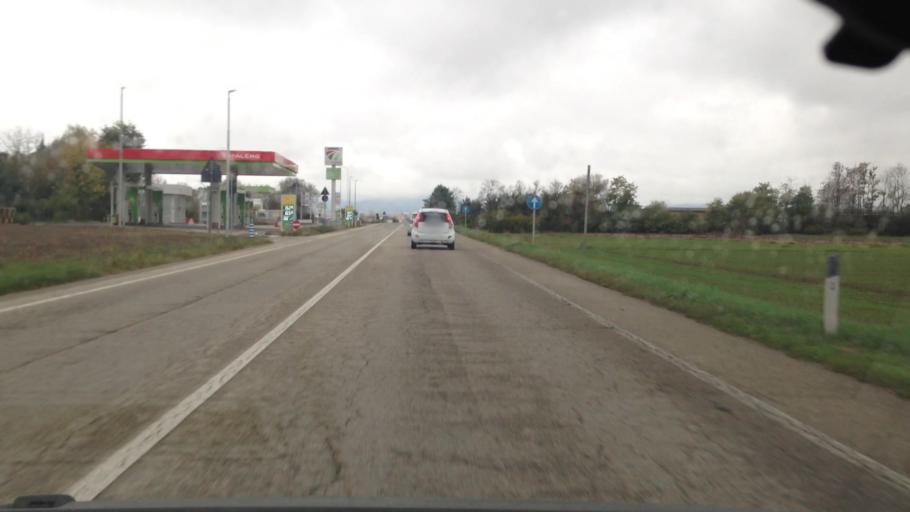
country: IT
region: Piedmont
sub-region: Provincia di Torino
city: Riva Presso Chieri
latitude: 44.9905
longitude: 7.8679
